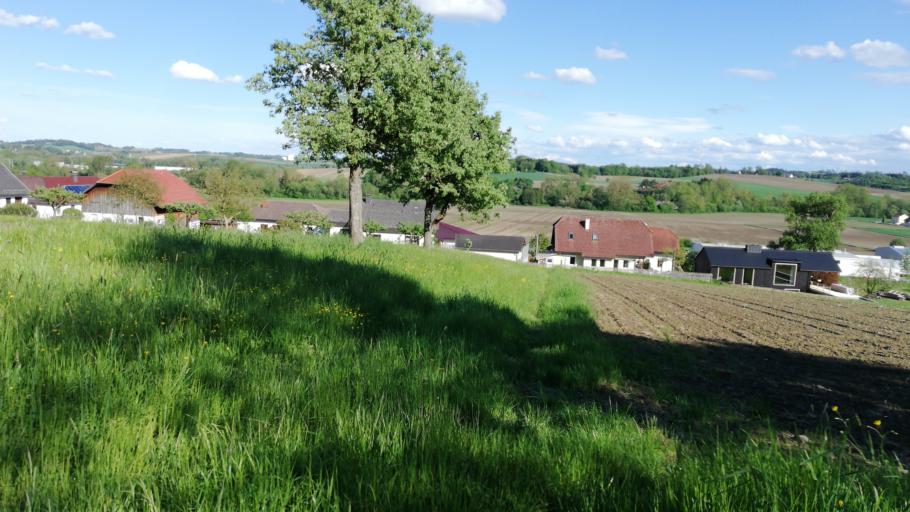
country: AT
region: Upper Austria
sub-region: Politischer Bezirk Grieskirchen
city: Bad Schallerbach
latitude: 48.2204
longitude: 13.9285
